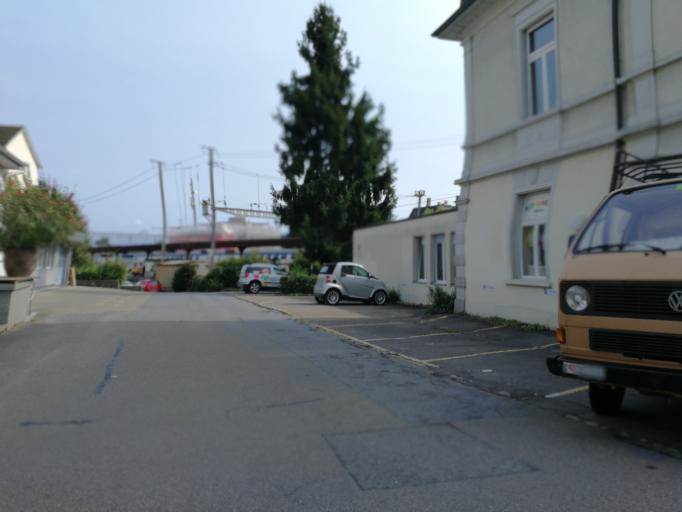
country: CH
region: Zurich
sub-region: Bezirk Meilen
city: Stafa
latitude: 47.2412
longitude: 8.7204
